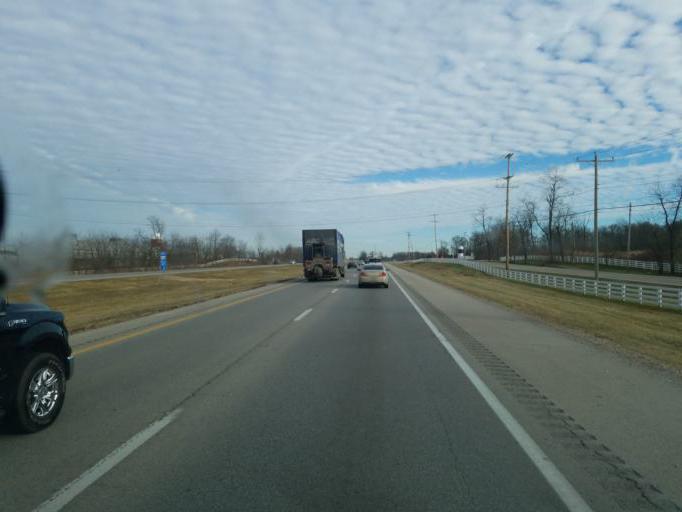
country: US
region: Ohio
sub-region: Franklin County
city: New Albany
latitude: 40.0796
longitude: -82.7710
